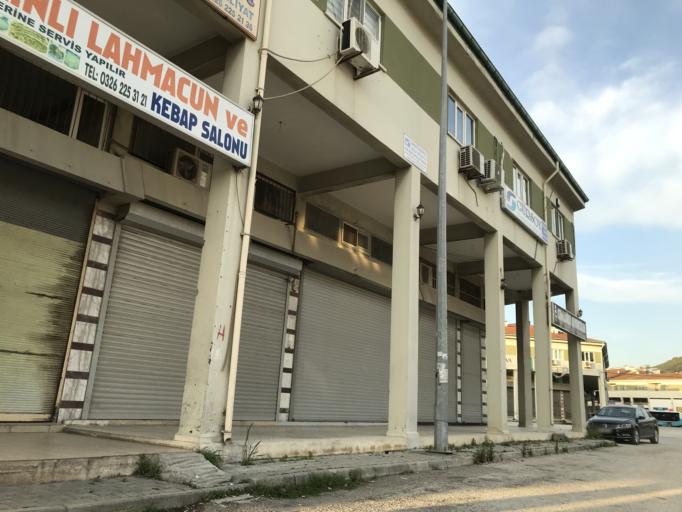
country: TR
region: Hatay
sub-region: Antakya Ilcesi
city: Antakya
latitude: 36.2125
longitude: 36.1645
